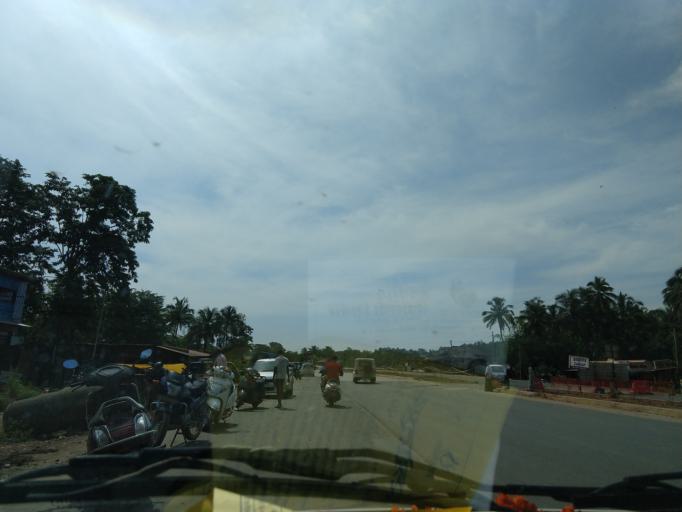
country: IN
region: Maharashtra
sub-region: Sindhudurg
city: Kudal
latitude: 15.9515
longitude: 73.7393
